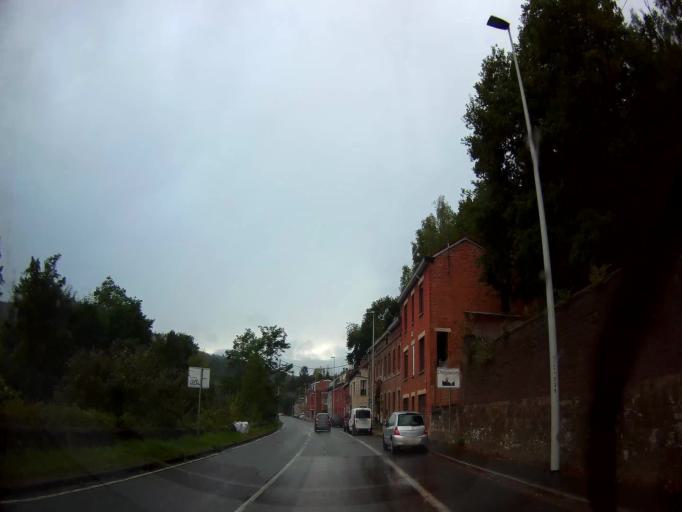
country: BE
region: Wallonia
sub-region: Province de Liege
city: Chaudfontaine
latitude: 50.5817
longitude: 5.6640
